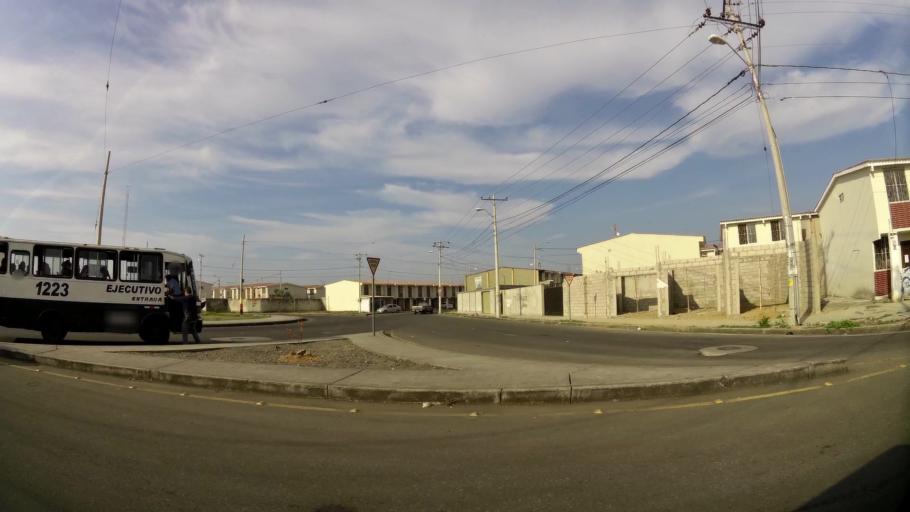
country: EC
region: Guayas
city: Eloy Alfaro
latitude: -2.0636
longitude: -79.8945
